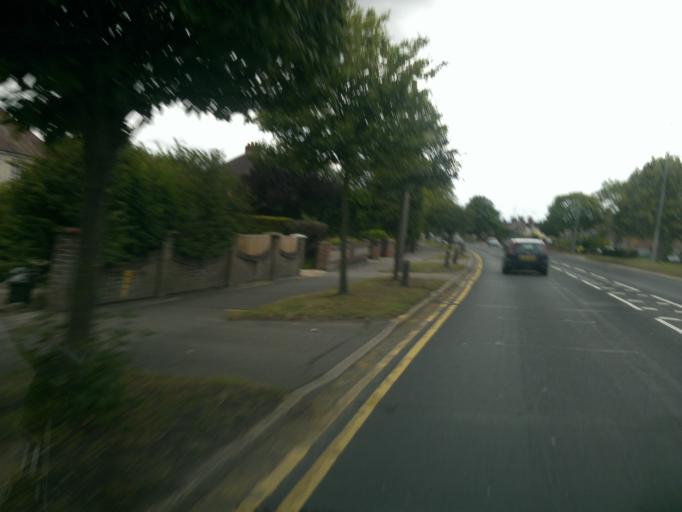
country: GB
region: England
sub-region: Essex
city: Colchester
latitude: 51.9072
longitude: 0.9248
